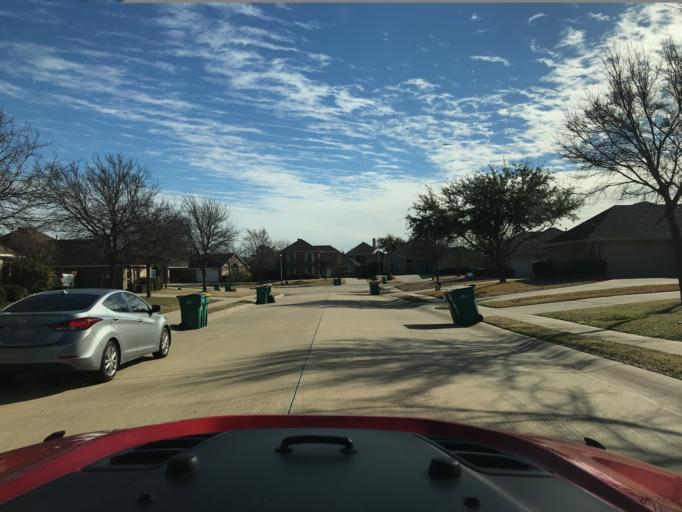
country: US
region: Texas
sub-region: Denton County
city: Lewisville
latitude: 33.0468
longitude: -97.0342
